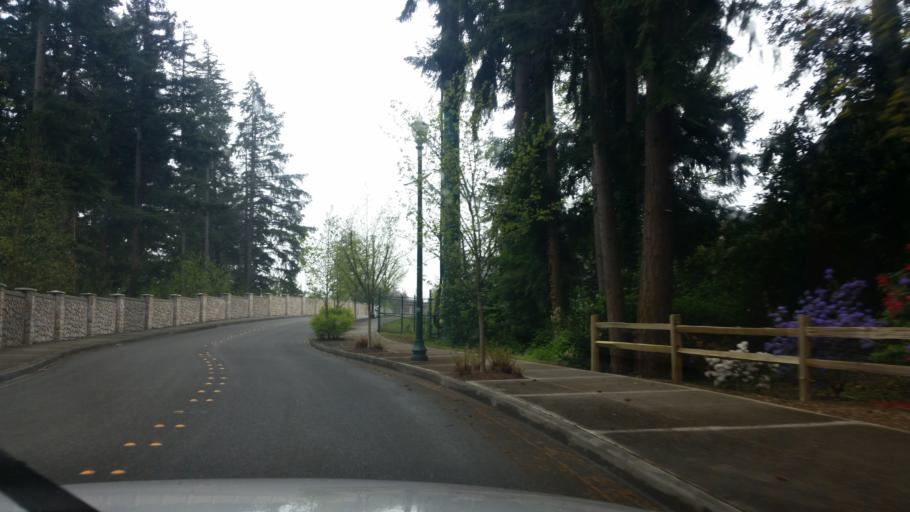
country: US
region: Washington
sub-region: Pierce County
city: University Place
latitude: 47.2229
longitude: -122.5351
